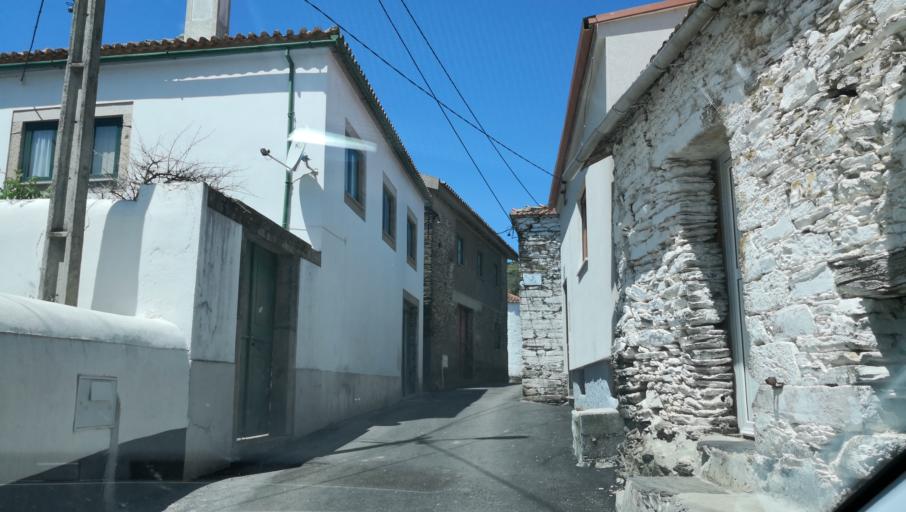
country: PT
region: Vila Real
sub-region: Vila Real
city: Vila Real
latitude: 41.2265
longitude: -7.7202
